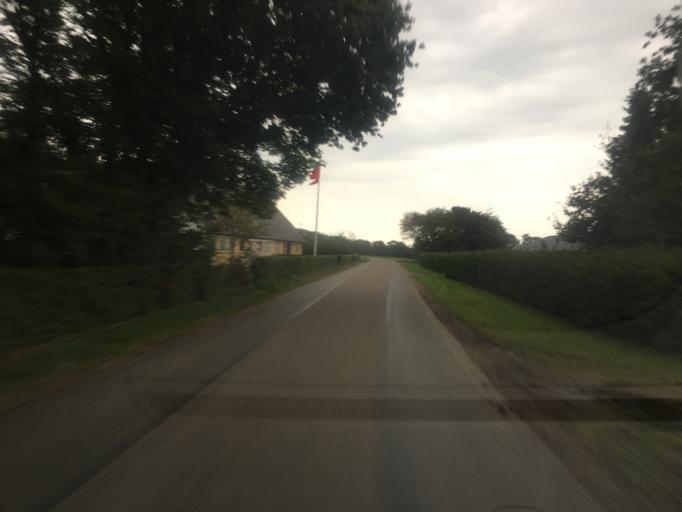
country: DK
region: South Denmark
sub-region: Tonder Kommune
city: Logumkloster
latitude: 54.9983
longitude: 9.0177
